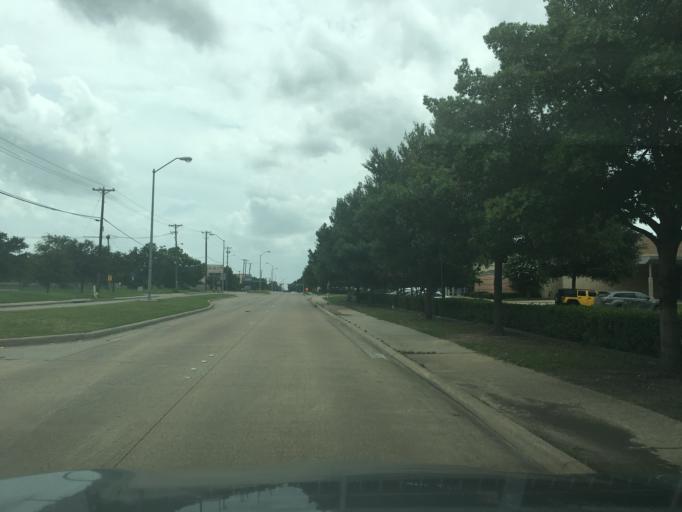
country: US
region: Texas
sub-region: Dallas County
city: Richardson
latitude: 32.9376
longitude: -96.7310
